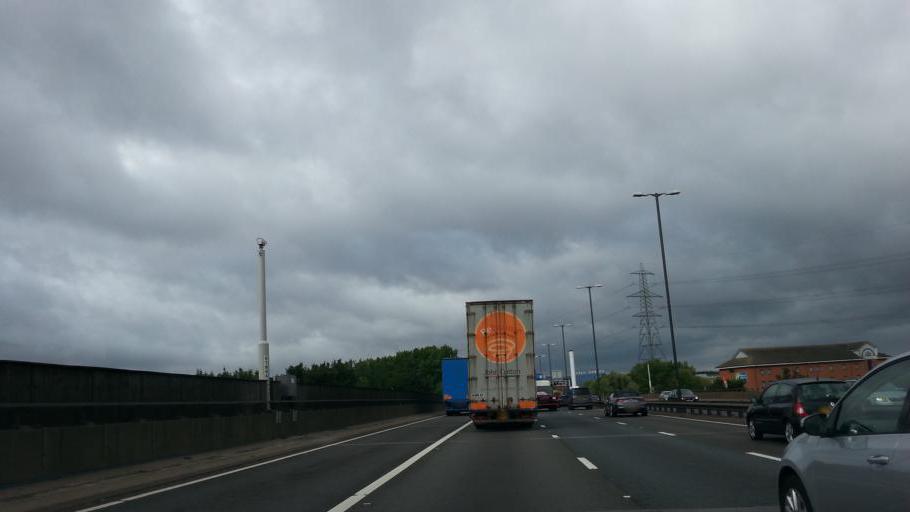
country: GB
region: England
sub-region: Warwickshire
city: Water Orton
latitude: 52.5091
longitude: -1.7947
